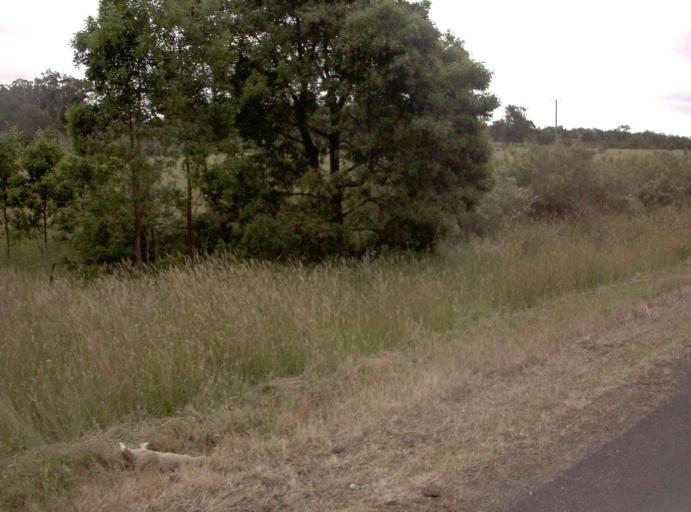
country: AU
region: Victoria
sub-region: Wellington
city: Sale
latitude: -38.2419
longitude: 147.0549
